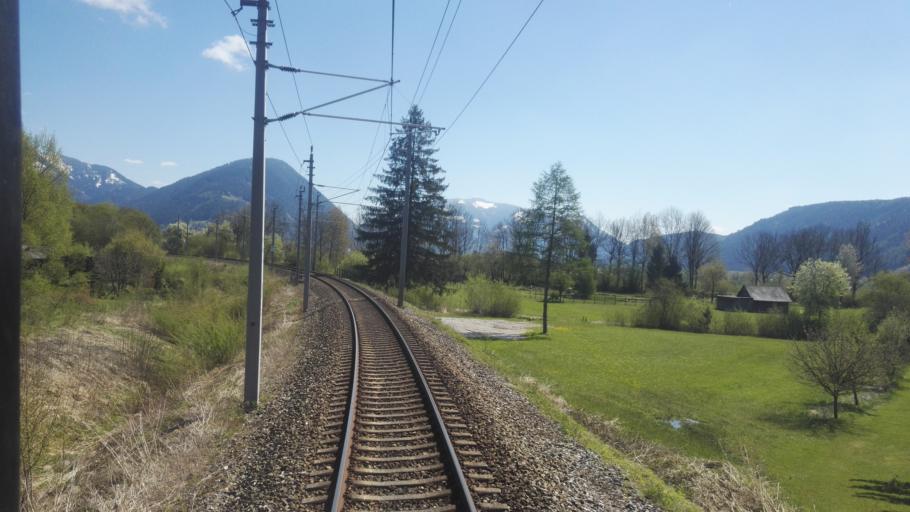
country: AT
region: Styria
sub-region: Politischer Bezirk Liezen
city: Weissenbach bei Liezen
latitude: 47.5631
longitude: 14.2049
